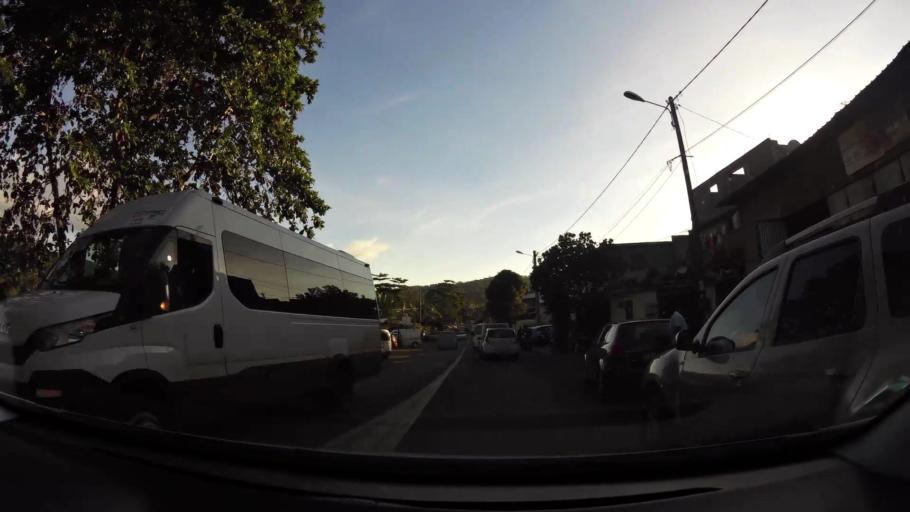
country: YT
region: Dembeni
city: Dembeni
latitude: -12.8368
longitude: 45.1768
